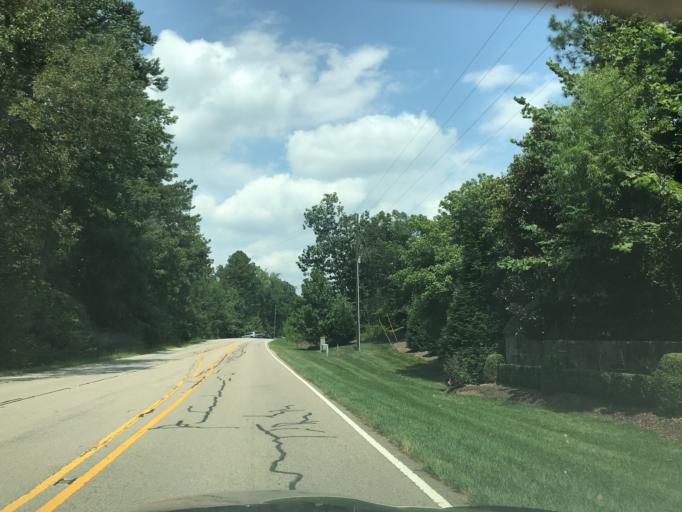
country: US
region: North Carolina
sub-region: Wake County
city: Cary
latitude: 35.8415
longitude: -78.7238
